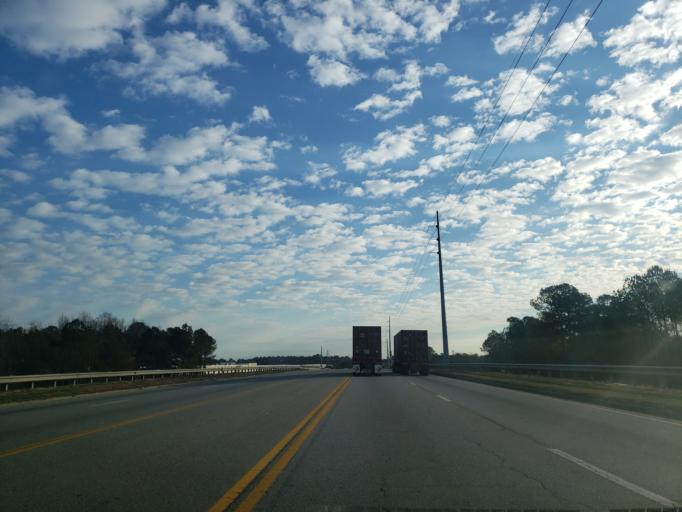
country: US
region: Georgia
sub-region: Chatham County
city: Port Wentworth
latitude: 32.1640
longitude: -81.2023
